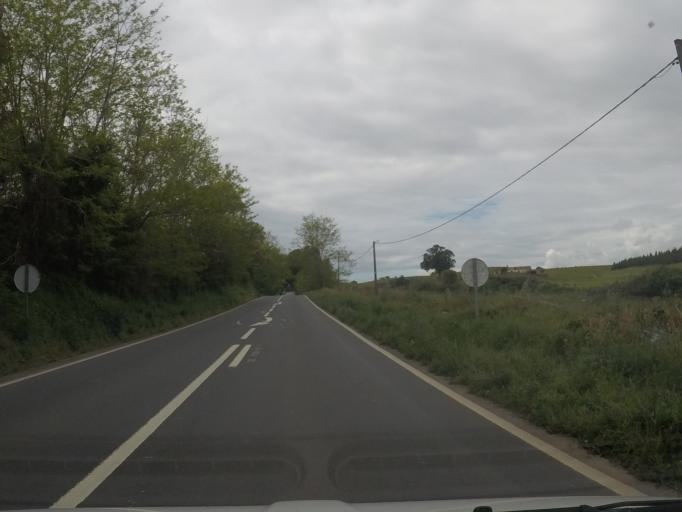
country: PT
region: Setubal
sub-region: Santiago do Cacem
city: Cercal
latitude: 37.8213
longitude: -8.6859
